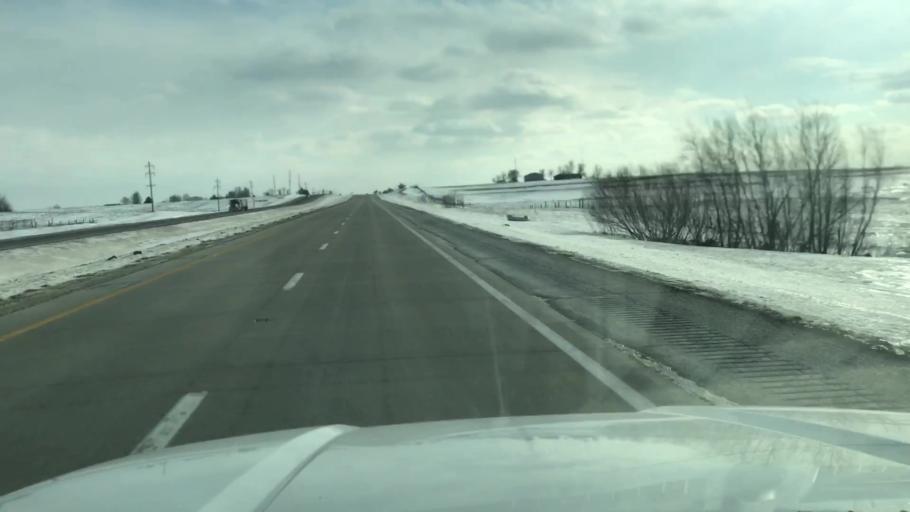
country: US
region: Missouri
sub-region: Nodaway County
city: Maryville
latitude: 40.2658
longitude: -94.8670
